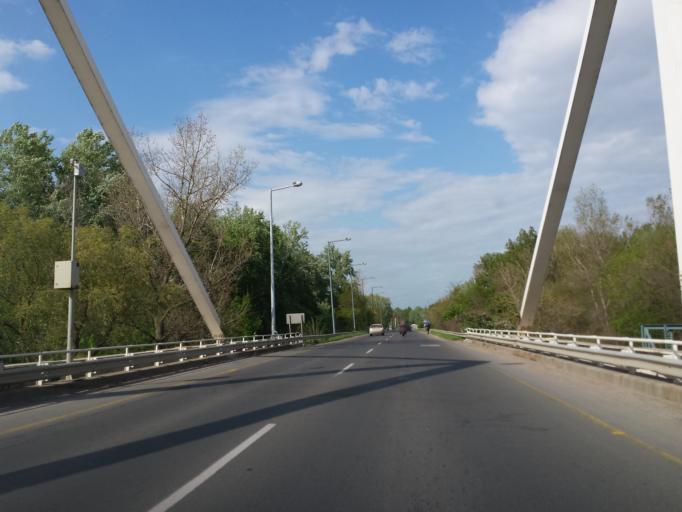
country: HU
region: Csongrad
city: Kiszombor
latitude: 46.2029
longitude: 20.4536
